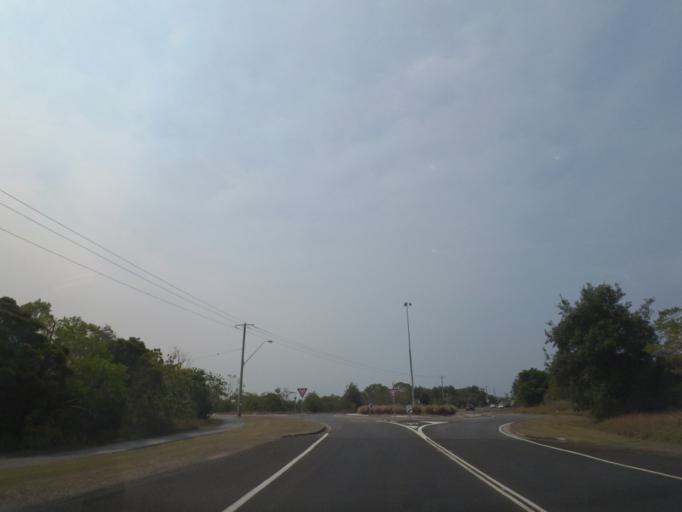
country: AU
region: New South Wales
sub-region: Tweed
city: Casuarina
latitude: -28.3419
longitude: 153.5715
